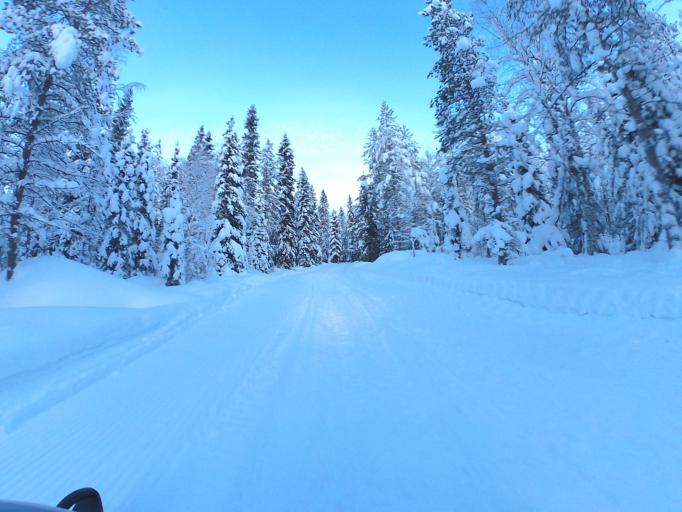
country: FI
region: Lapland
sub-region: Rovaniemi
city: Rovaniemi
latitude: 66.5168
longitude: 26.0046
